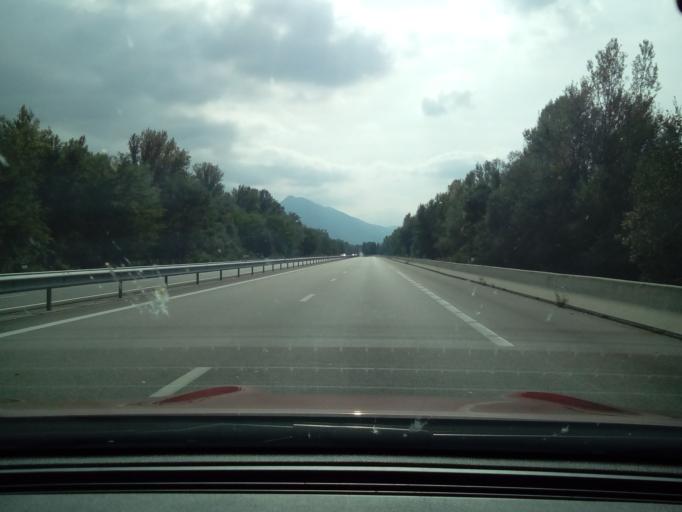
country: FR
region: Rhone-Alpes
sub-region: Departement de l'Isere
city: Saint-Quentin-sur-Isere
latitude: 45.2569
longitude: 5.5104
